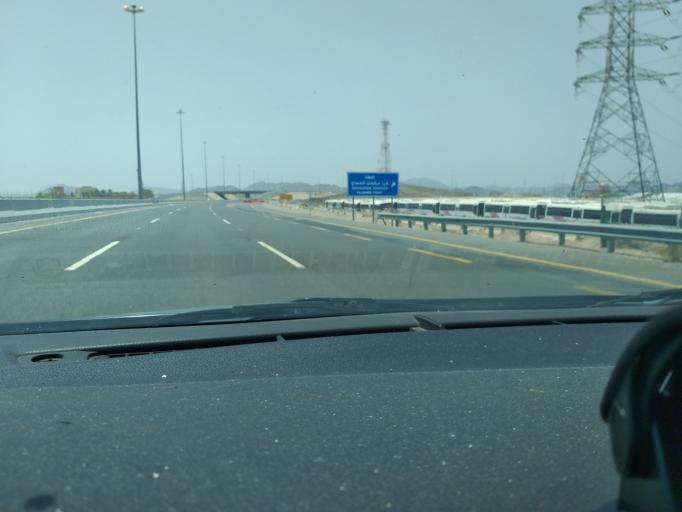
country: SA
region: Makkah
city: Mecca
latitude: 21.3262
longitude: 39.9724
